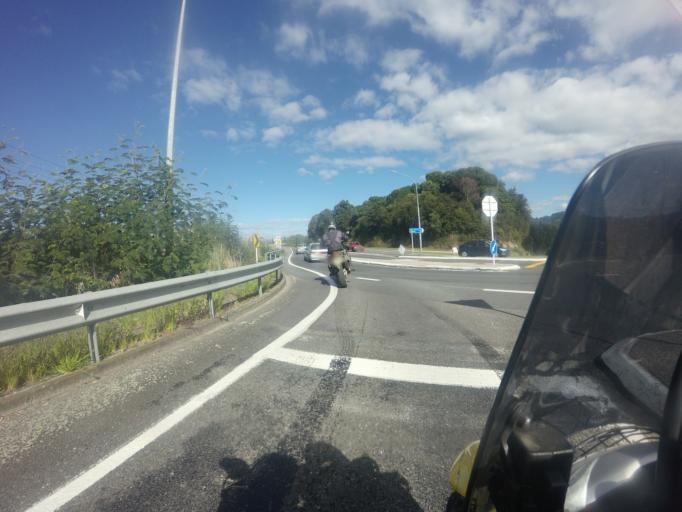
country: NZ
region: Bay of Plenty
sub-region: Whakatane District
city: Whakatane
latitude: -37.9625
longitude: 177.0061
